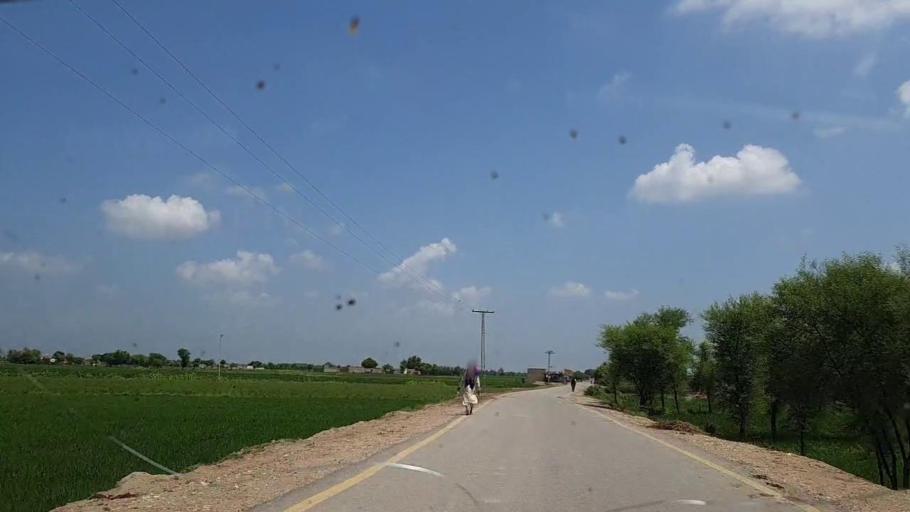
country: PK
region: Sindh
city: Tharu Shah
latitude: 26.9840
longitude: 68.0798
